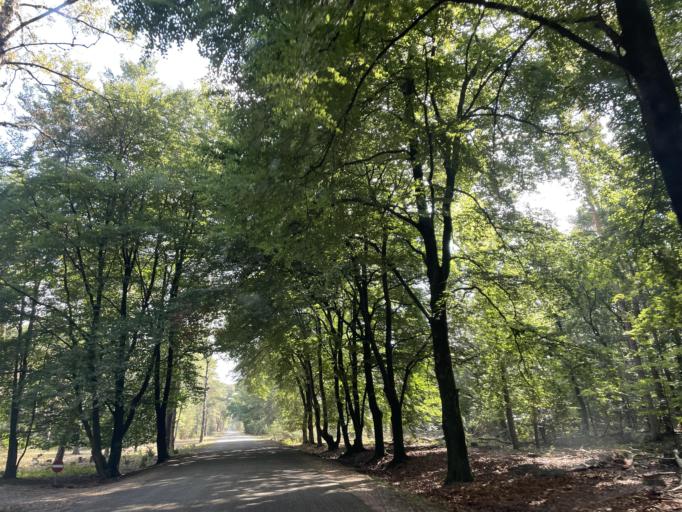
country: NL
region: Gelderland
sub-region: Gemeente Ede
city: Otterlo
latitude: 52.1016
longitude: 5.7921
